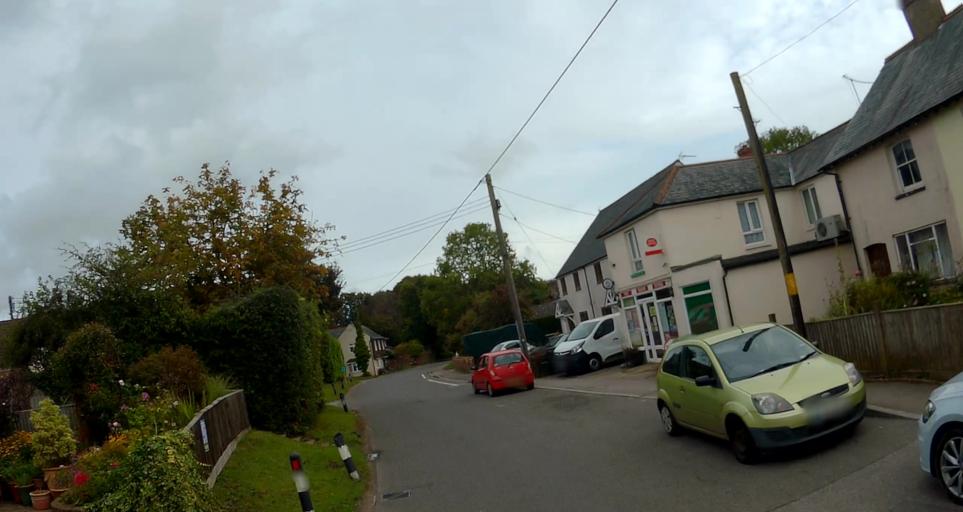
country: GB
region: England
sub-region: Hampshire
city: Four Marks
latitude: 51.1295
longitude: -1.0645
